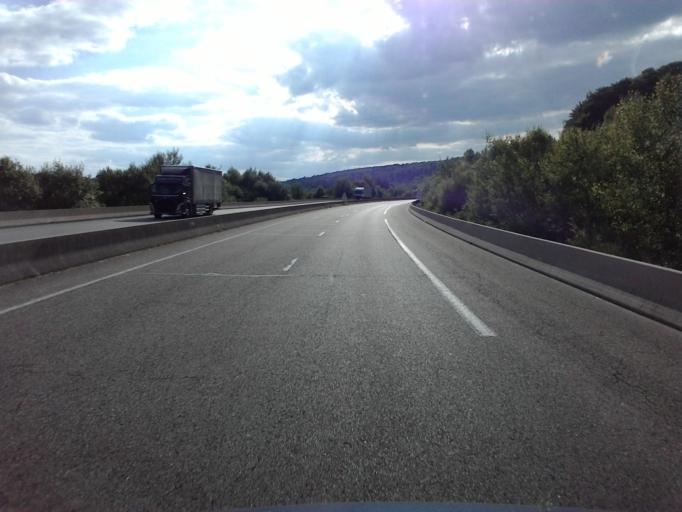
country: FR
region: Lorraine
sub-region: Departement des Vosges
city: Plombieres-les-Bains
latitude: 47.9863
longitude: 6.5165
